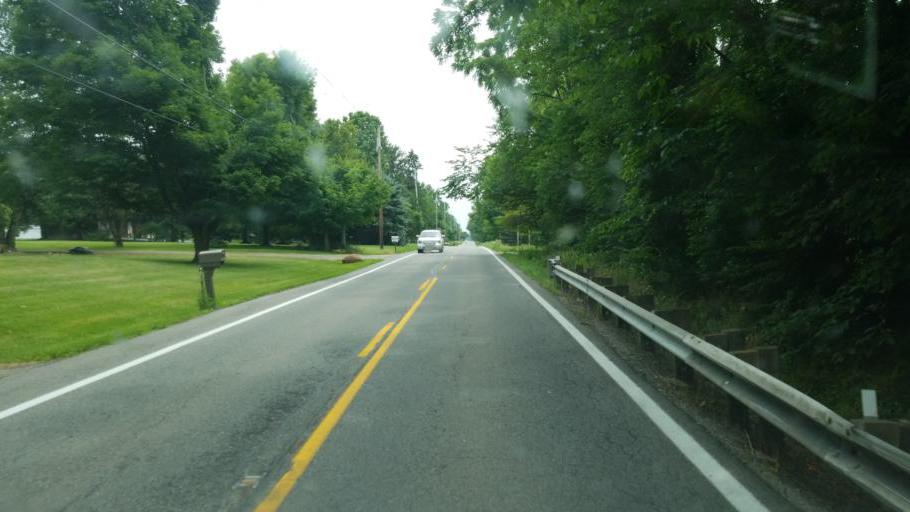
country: US
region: Ohio
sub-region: Trumbull County
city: Cortland
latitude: 41.3767
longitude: -80.7369
